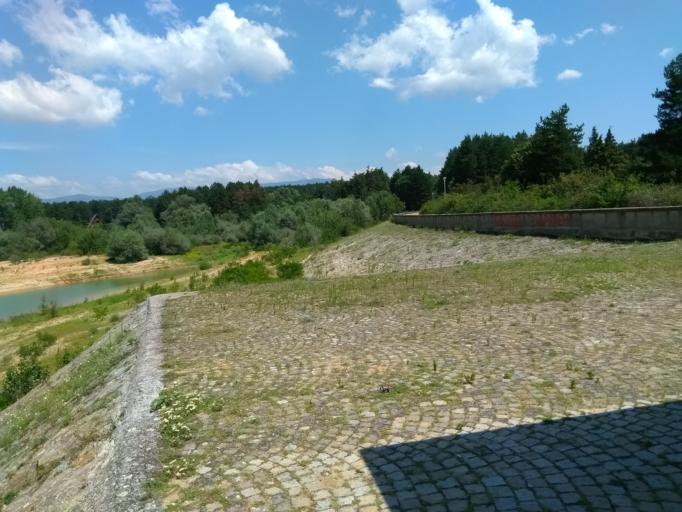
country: BG
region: Stara Zagora
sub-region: Obshtina Kazanluk
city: Kazanluk
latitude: 42.6155
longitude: 25.3223
